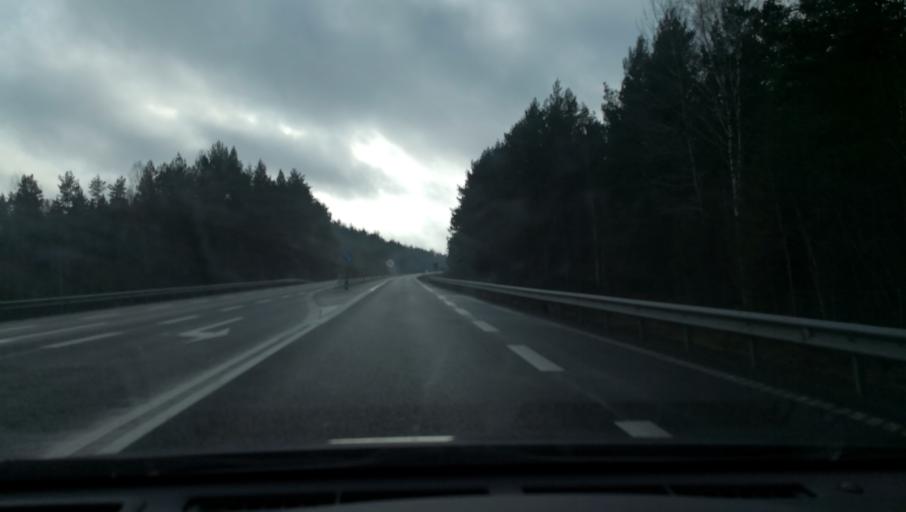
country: SE
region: Vaestra Goetaland
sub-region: Gullspangs Kommun
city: Anderstorp
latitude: 58.9274
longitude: 14.4157
